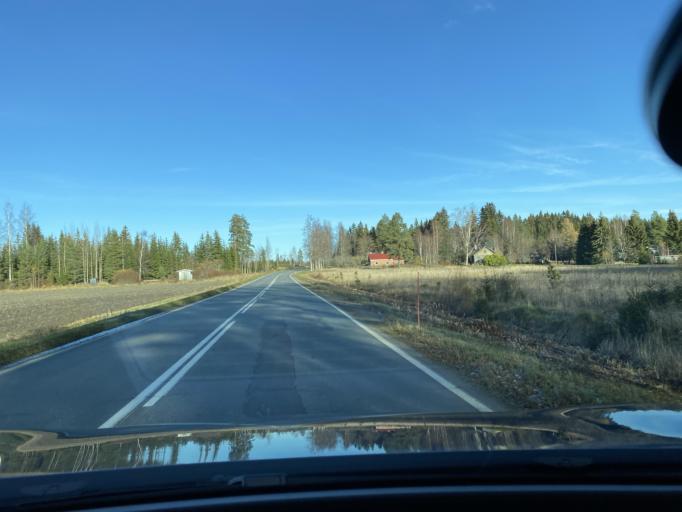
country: FI
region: Haeme
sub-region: Forssa
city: Tammela
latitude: 60.8486
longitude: 23.8396
